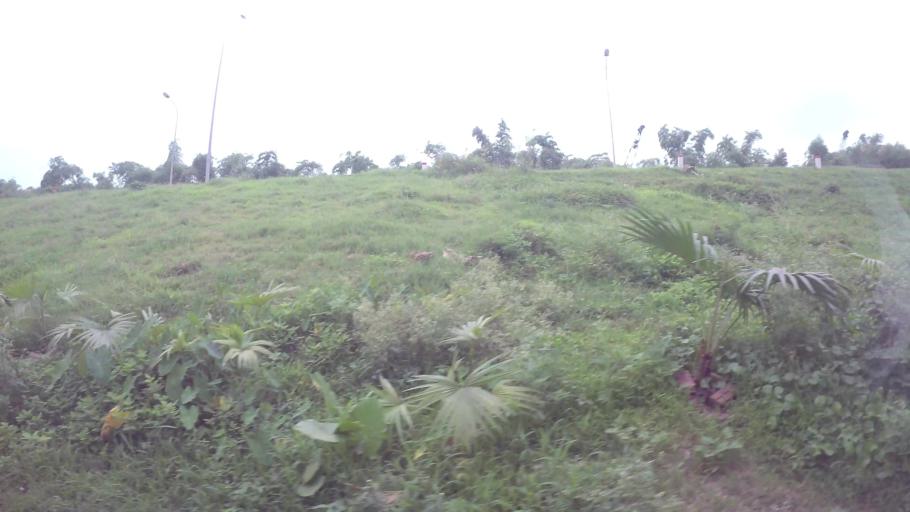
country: VN
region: Ha Noi
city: Trau Quy
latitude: 21.0473
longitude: 105.9279
